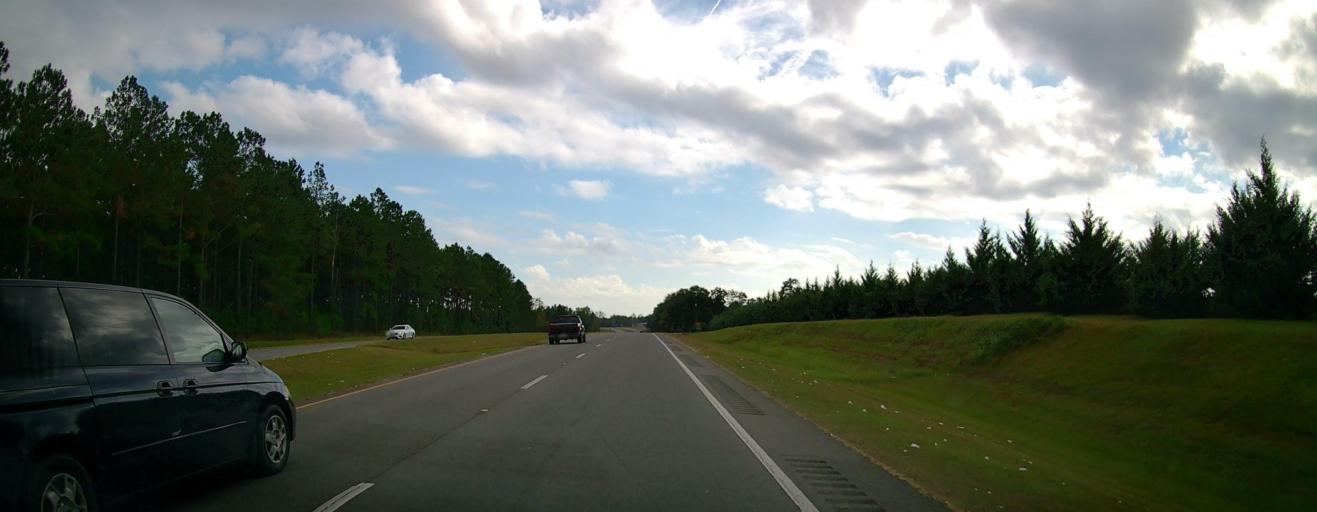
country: US
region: Georgia
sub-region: Thomas County
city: Meigs
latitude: 31.0558
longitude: -84.0718
